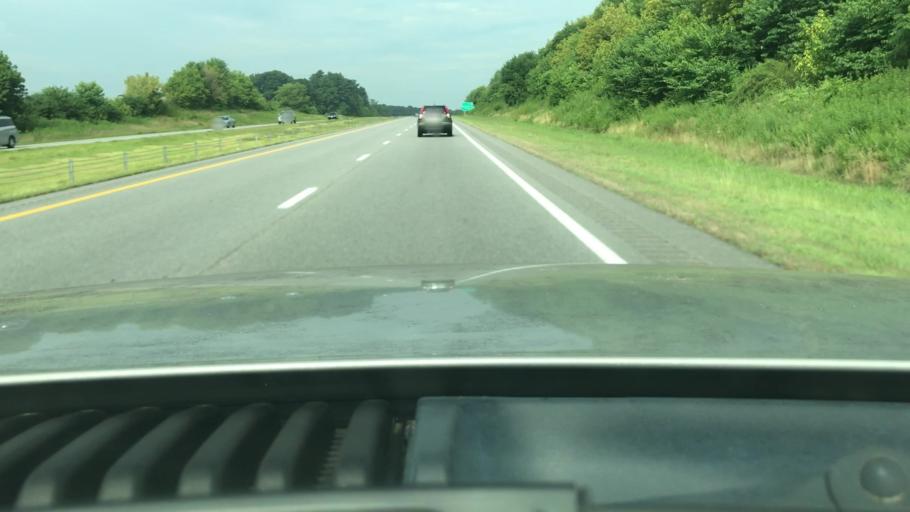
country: US
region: North Carolina
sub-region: Surry County
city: Elkin
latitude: 36.1611
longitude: -80.9520
